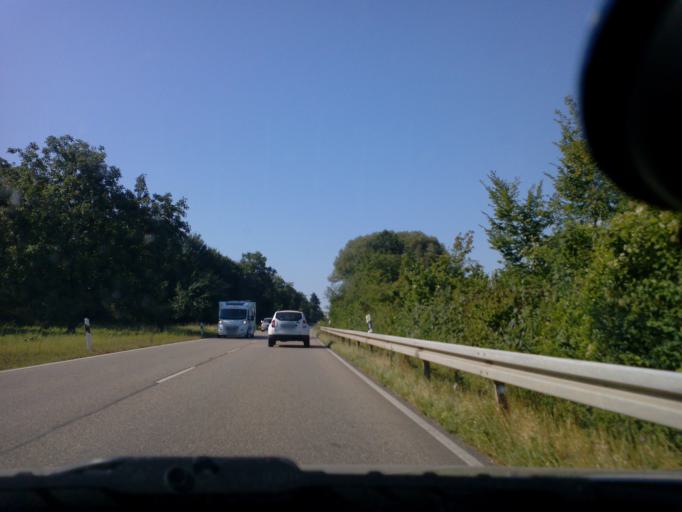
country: DE
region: Baden-Wuerttemberg
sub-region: Karlsruhe Region
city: Weingarten
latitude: 49.0659
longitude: 8.5383
